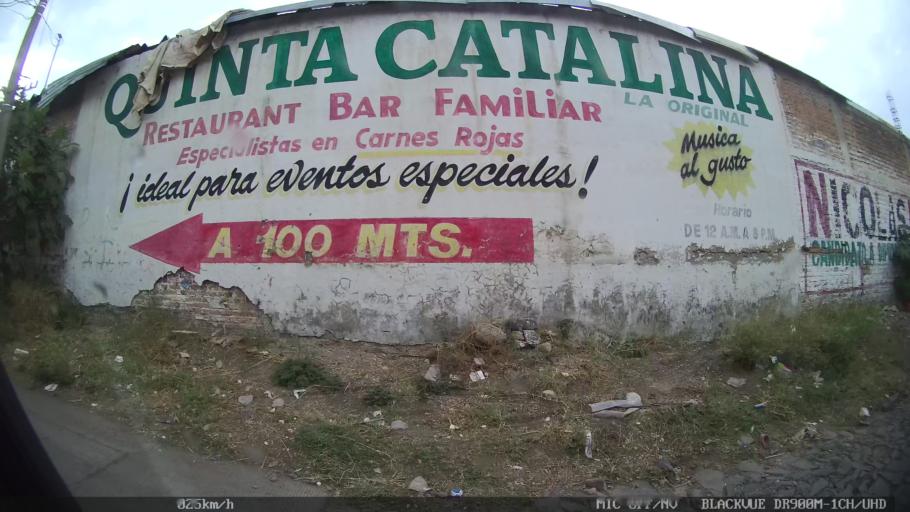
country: MX
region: Jalisco
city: Tlaquepaque
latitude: 20.6208
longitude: -103.2709
